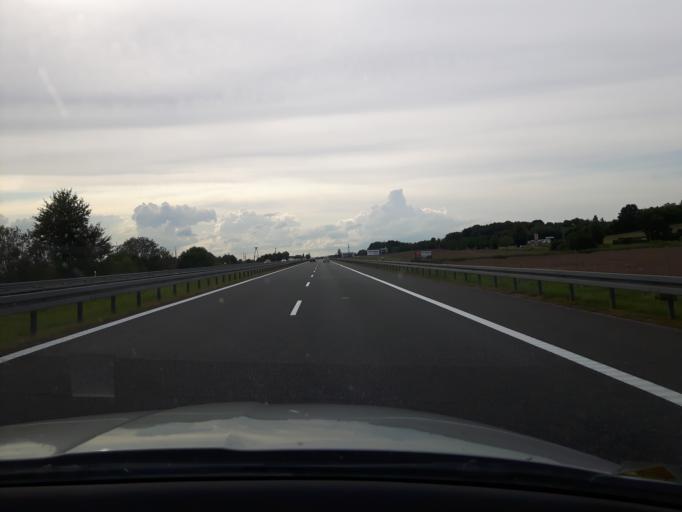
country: PL
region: Warmian-Masurian Voivodeship
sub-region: Powiat elblaski
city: Gronowo Gorne
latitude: 54.1064
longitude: 19.5044
